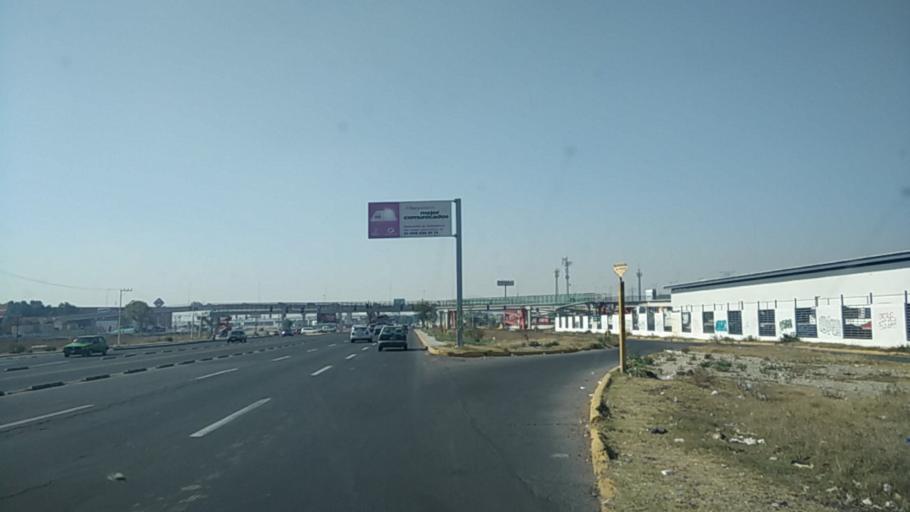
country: MX
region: Mexico
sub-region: Atenco
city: Colonia el Salado
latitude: 19.5905
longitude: -99.0230
